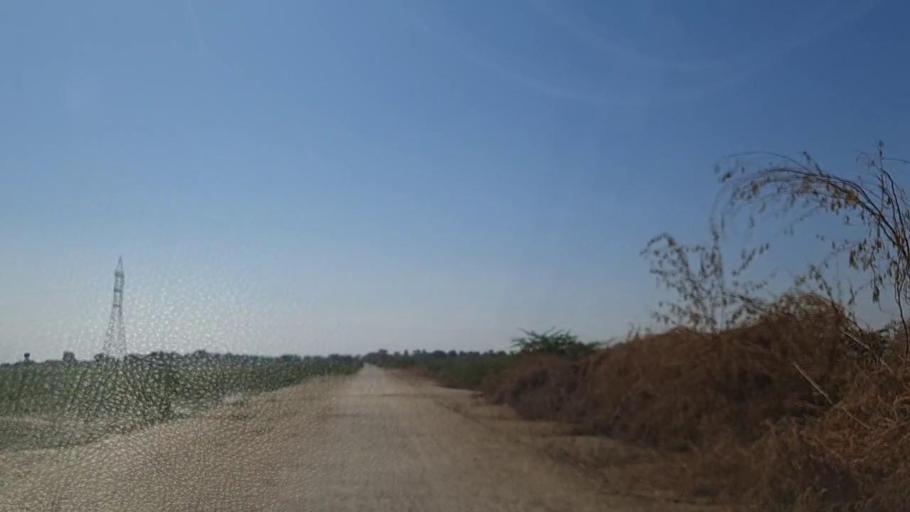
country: PK
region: Sindh
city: Kunri
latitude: 25.2970
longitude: 69.5367
